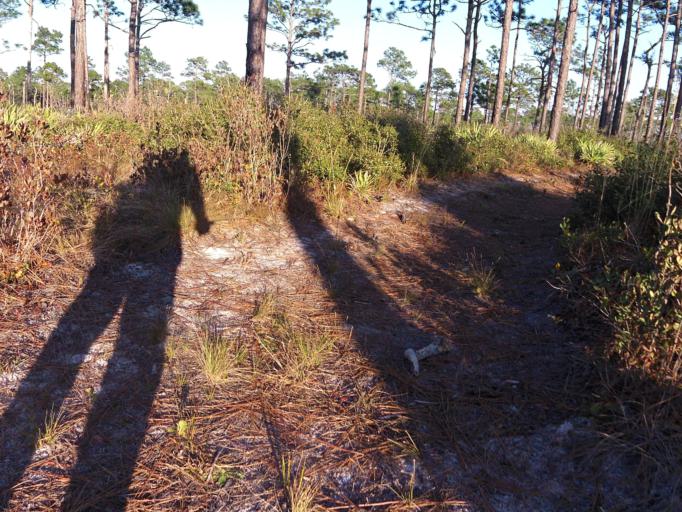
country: US
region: Florida
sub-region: Duval County
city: Atlantic Beach
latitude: 30.4767
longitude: -81.5036
